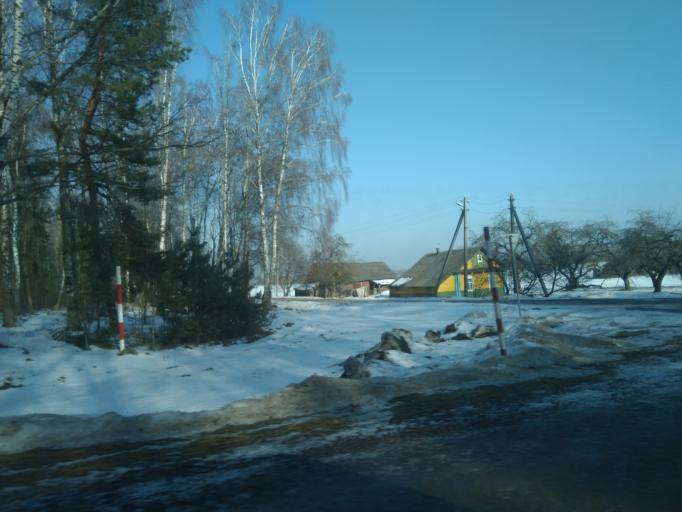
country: BY
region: Minsk
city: Snow
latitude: 53.2143
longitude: 26.4490
